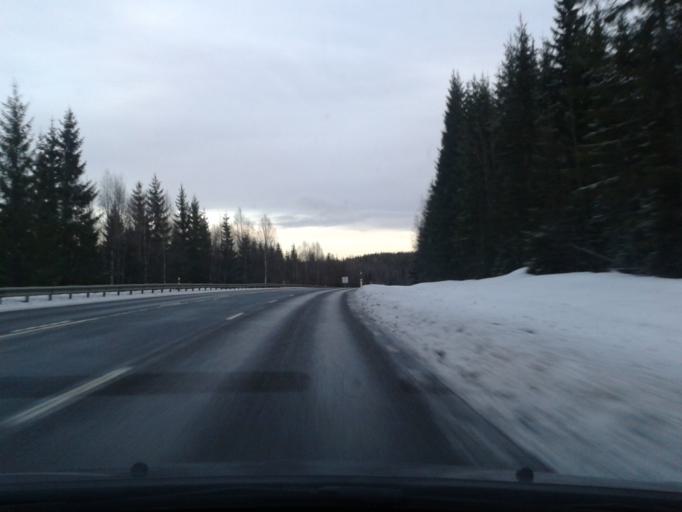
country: SE
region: Vaesternorrland
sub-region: Solleftea Kommun
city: Solleftea
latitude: 63.1320
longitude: 17.4669
